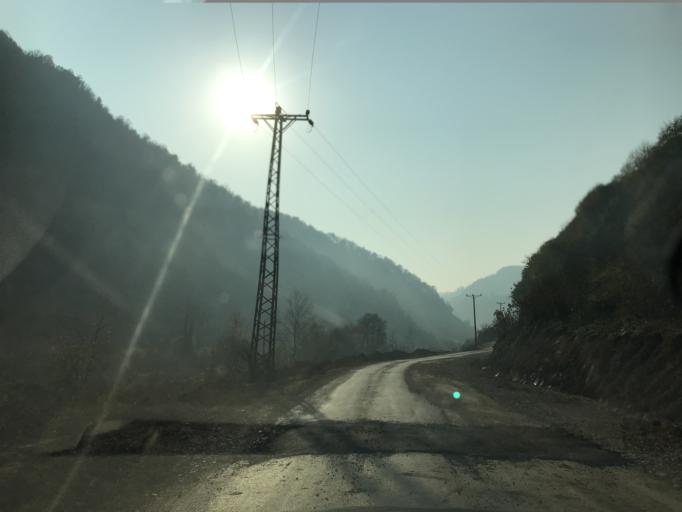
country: TR
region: Duzce
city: Cumayeri
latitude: 40.9275
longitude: 30.9297
